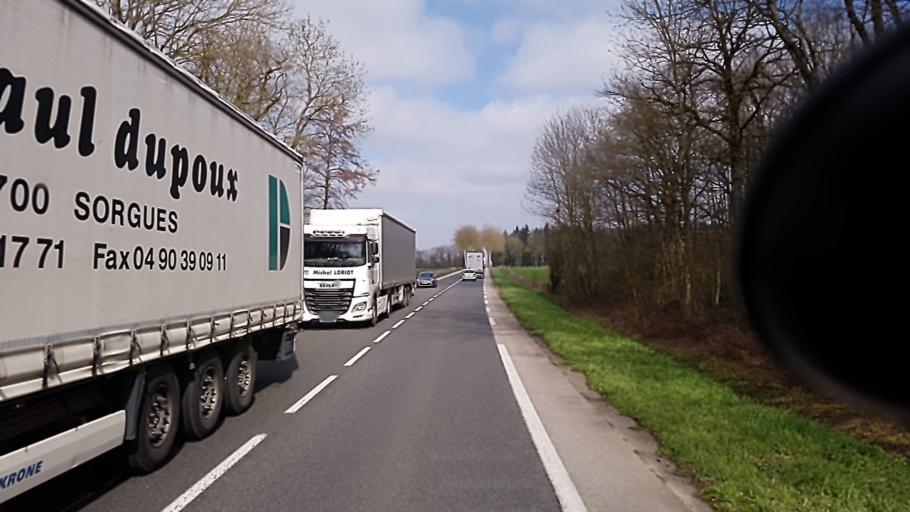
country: FR
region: Rhone-Alpes
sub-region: Departement de l'Ain
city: Saint-Paul-de-Varax
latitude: 46.0785
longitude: 5.0993
